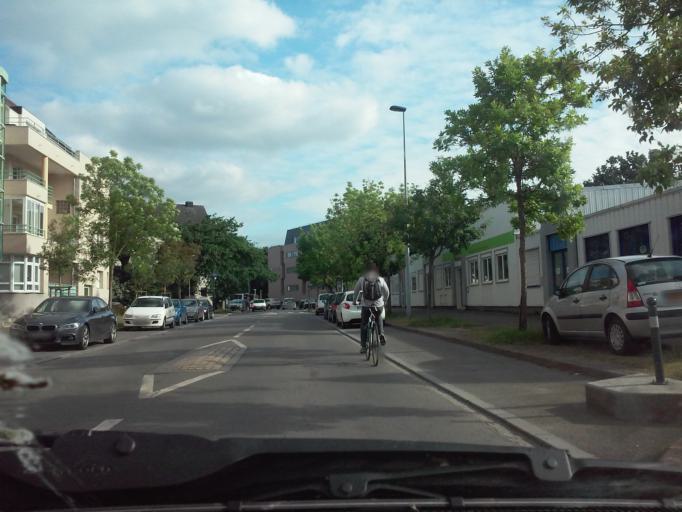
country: FR
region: Brittany
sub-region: Departement d'Ille-et-Vilaine
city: Saint-Jacques-de-la-Lande
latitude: 48.1024
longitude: -1.7121
